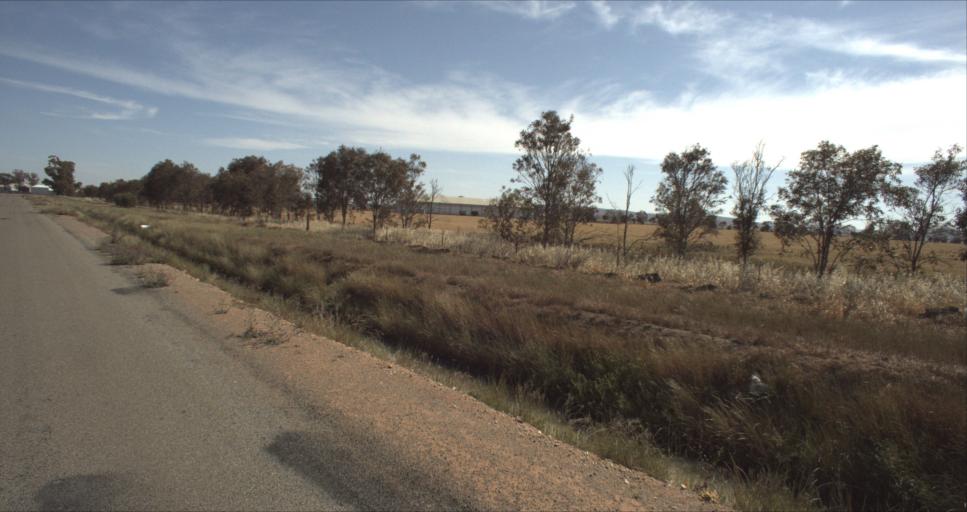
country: AU
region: New South Wales
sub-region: Leeton
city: Leeton
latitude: -34.5627
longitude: 146.4697
